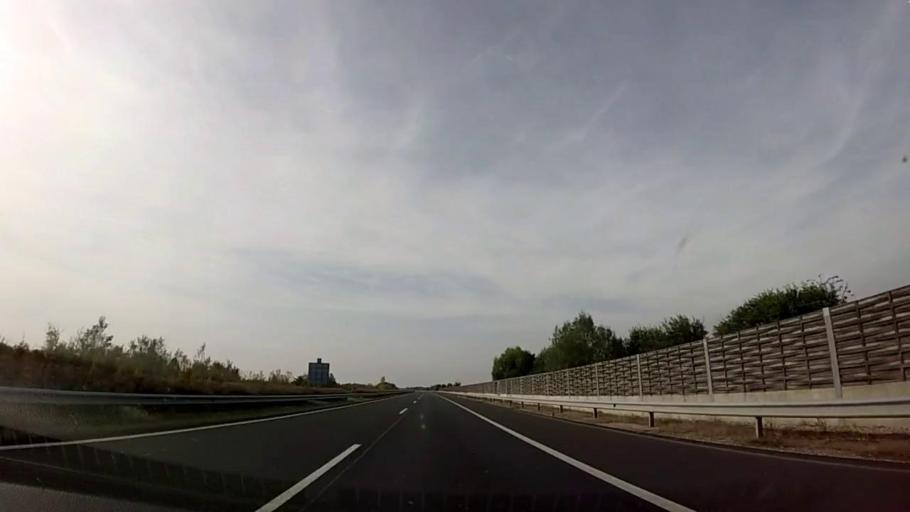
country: HU
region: Somogy
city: Fonyod
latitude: 46.7451
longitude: 17.6121
